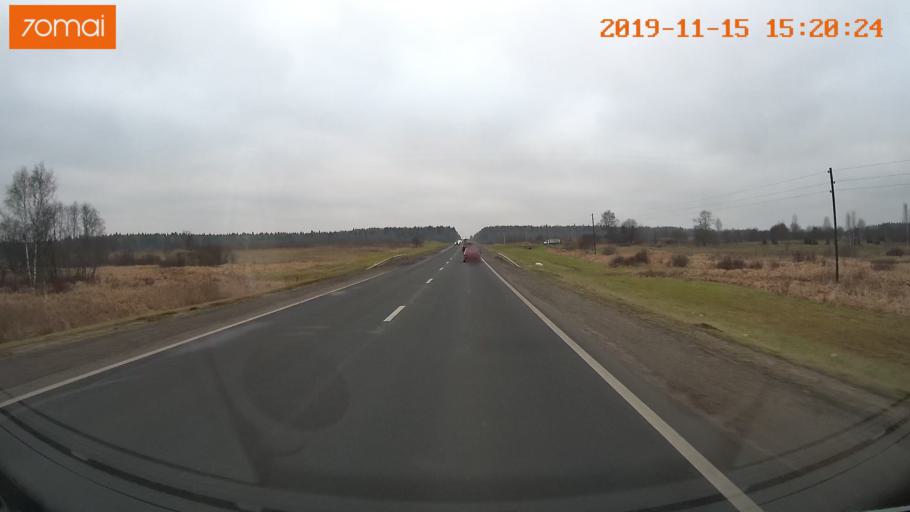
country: RU
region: Jaroslavl
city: Danilov
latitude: 58.2240
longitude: 40.1624
